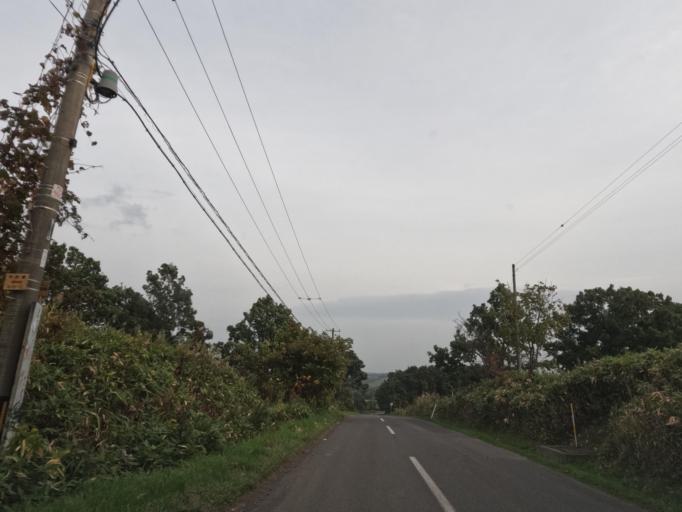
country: JP
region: Hokkaido
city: Date
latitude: 42.4064
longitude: 140.9223
